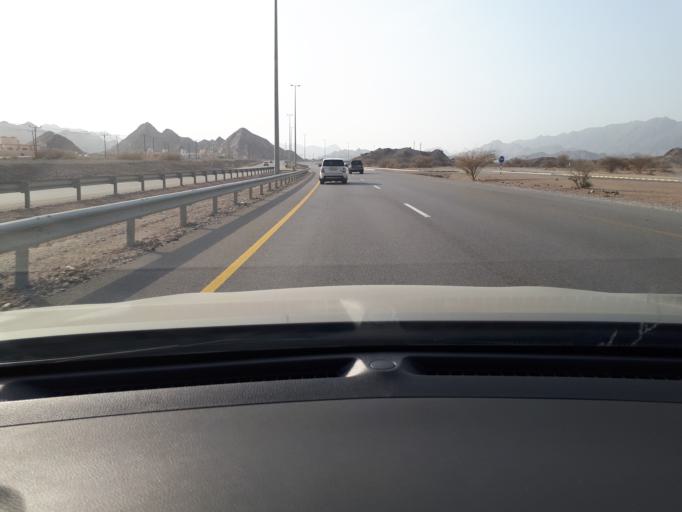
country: OM
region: Muhafazat Masqat
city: Muscat
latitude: 23.2847
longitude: 58.7477
